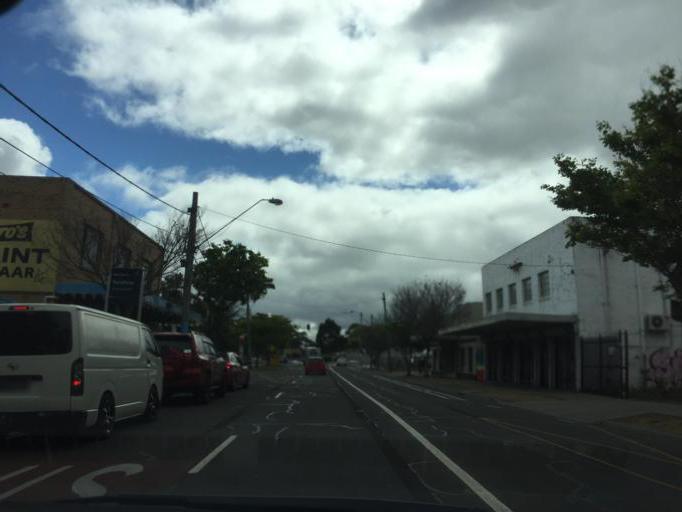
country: AU
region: Victoria
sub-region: Brimbank
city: Sunshine West
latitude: -37.7900
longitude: 144.8314
